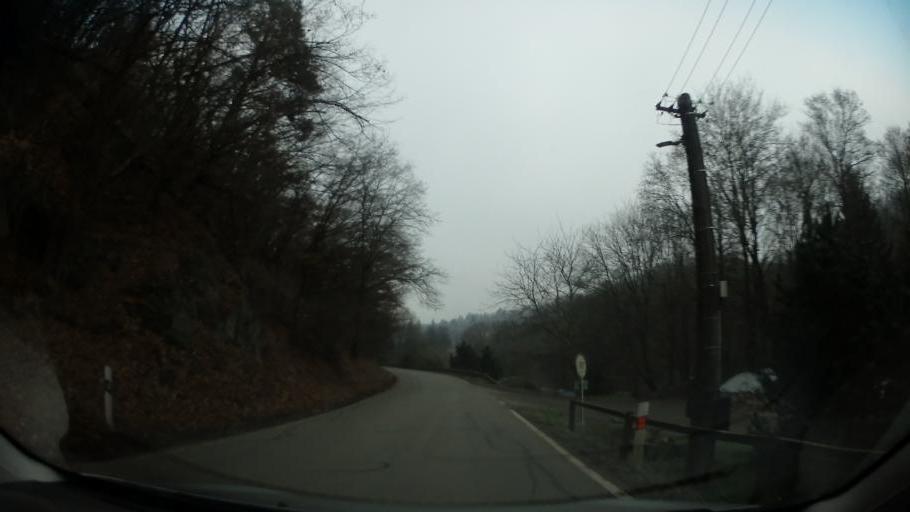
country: CZ
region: Vysocina
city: Mohelno
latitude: 49.1430
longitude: 16.2027
